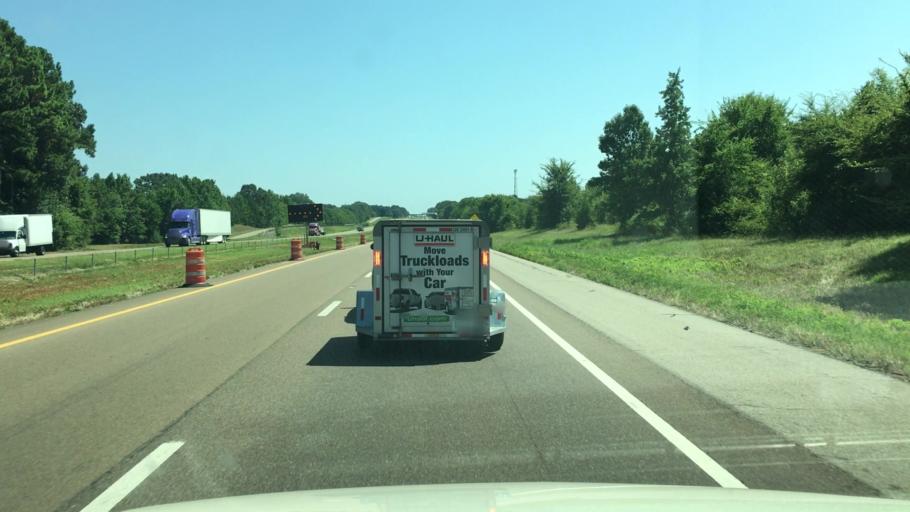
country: US
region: Texas
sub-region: Morris County
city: Omaha
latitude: 33.2548
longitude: -94.8420
